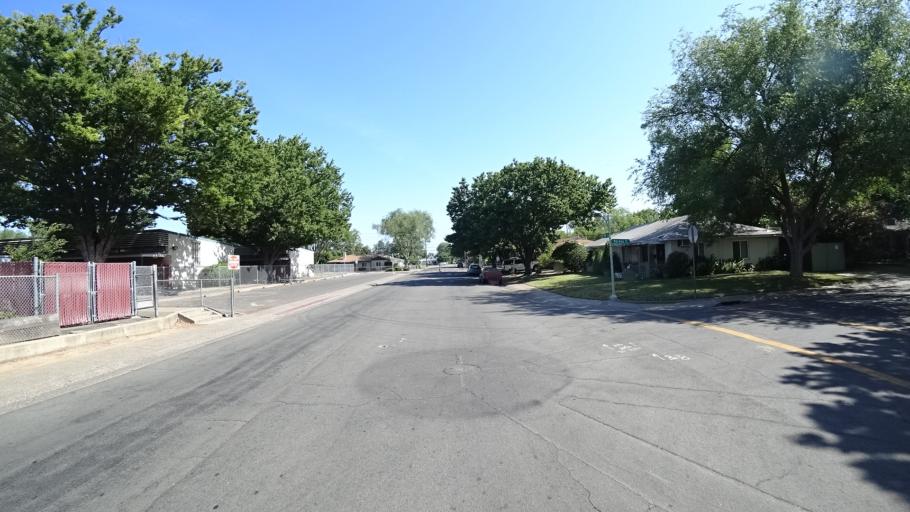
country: US
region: California
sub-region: Sacramento County
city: Parkway
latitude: 38.5305
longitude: -121.4387
